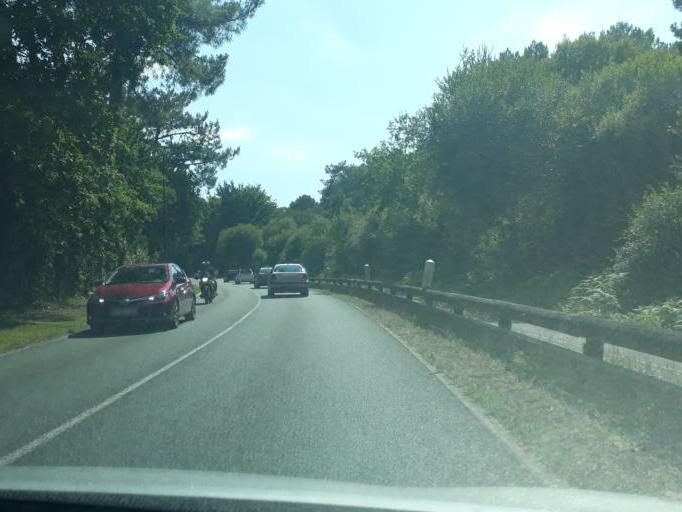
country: FR
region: Aquitaine
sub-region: Departement de la Gironde
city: Ares
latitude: 44.7370
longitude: -1.1952
